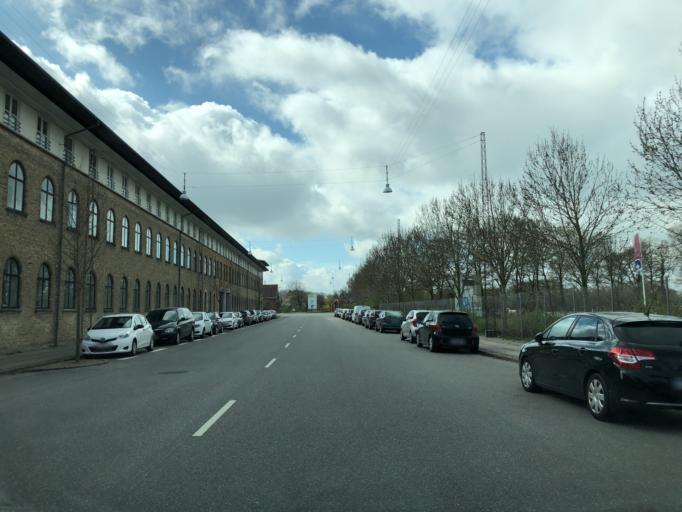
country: DK
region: North Denmark
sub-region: Alborg Kommune
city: Aalborg
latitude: 57.0532
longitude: 9.8918
